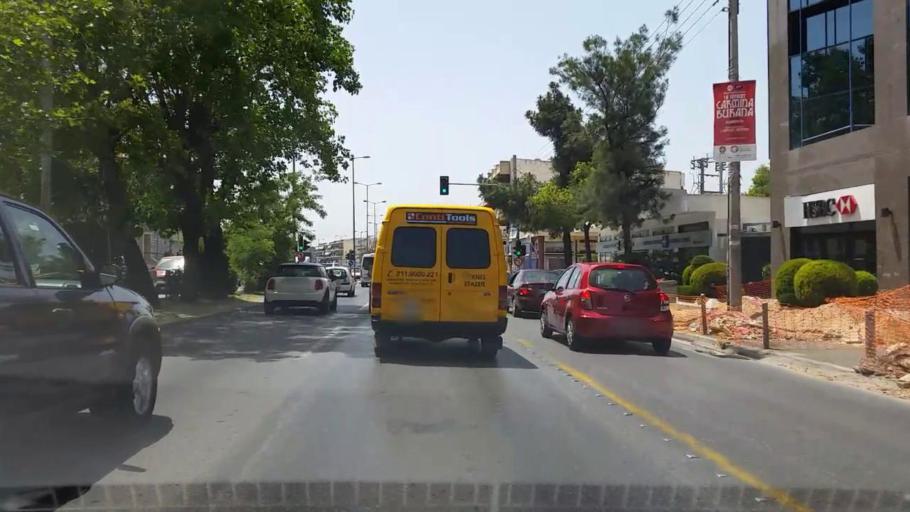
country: GR
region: Attica
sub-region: Nomarchia Athinas
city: Agia Paraskevi
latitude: 38.0138
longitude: 23.8224
